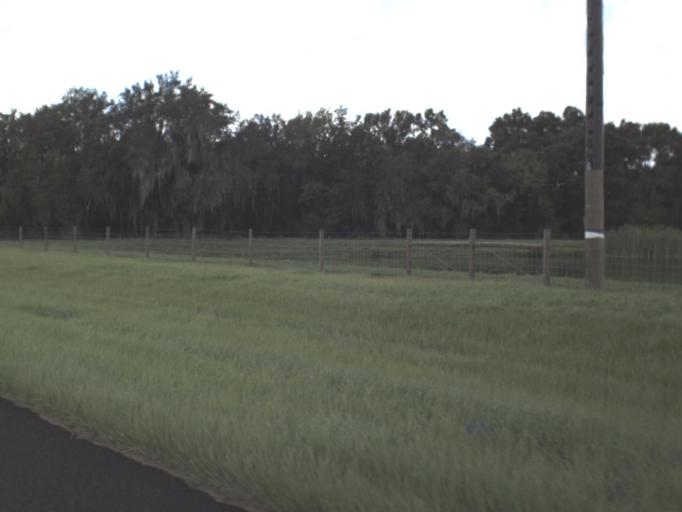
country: US
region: Florida
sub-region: Hardee County
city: Zolfo Springs
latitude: 27.4072
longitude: -81.7953
